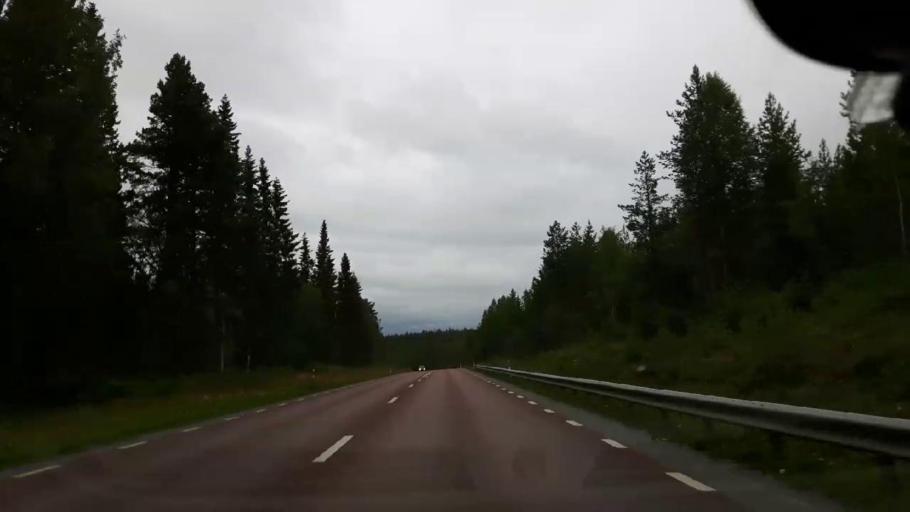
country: SE
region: Jaemtland
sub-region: Bergs Kommun
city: Hoverberg
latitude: 62.8308
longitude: 14.5189
